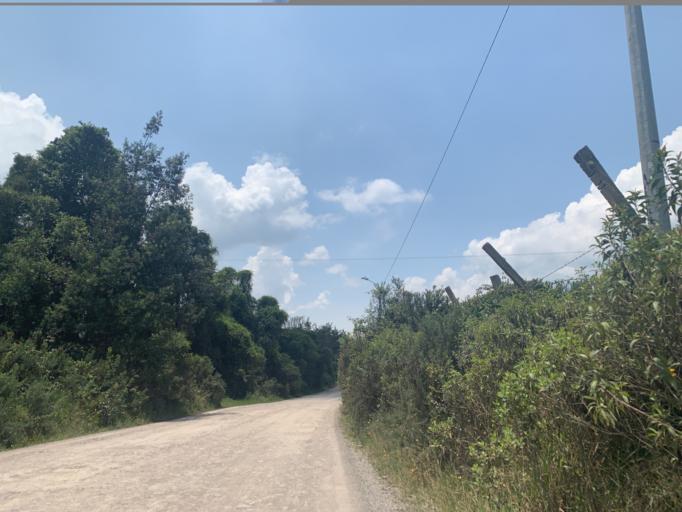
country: CO
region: Boyaca
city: Chiquinquira
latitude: 5.5929
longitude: -73.7585
